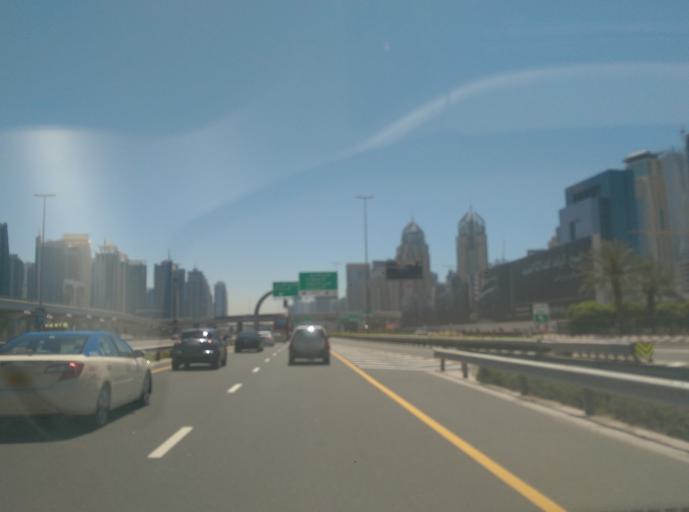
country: AE
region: Dubai
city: Dubai
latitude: 25.0891
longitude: 55.1570
